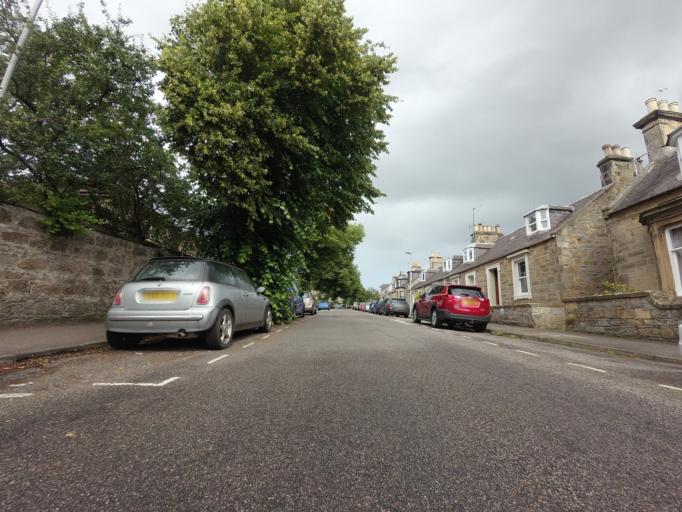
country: GB
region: Scotland
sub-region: Moray
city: Elgin
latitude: 57.6438
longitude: -3.3111
